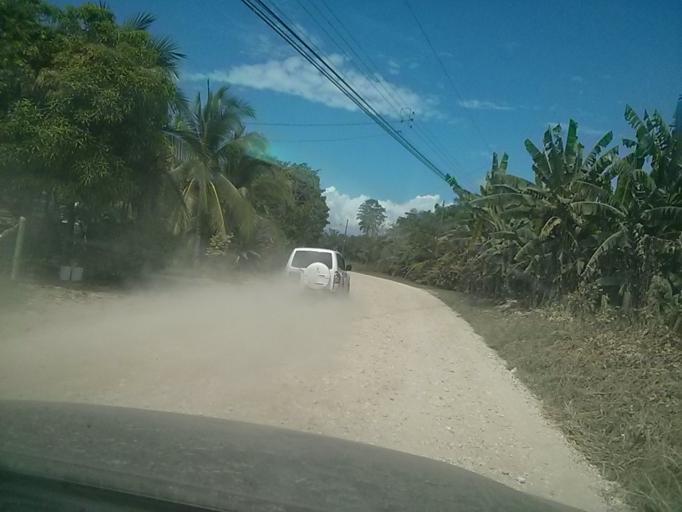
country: CR
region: Puntarenas
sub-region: Canton de Golfito
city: Golfito
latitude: 8.4585
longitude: -83.0492
